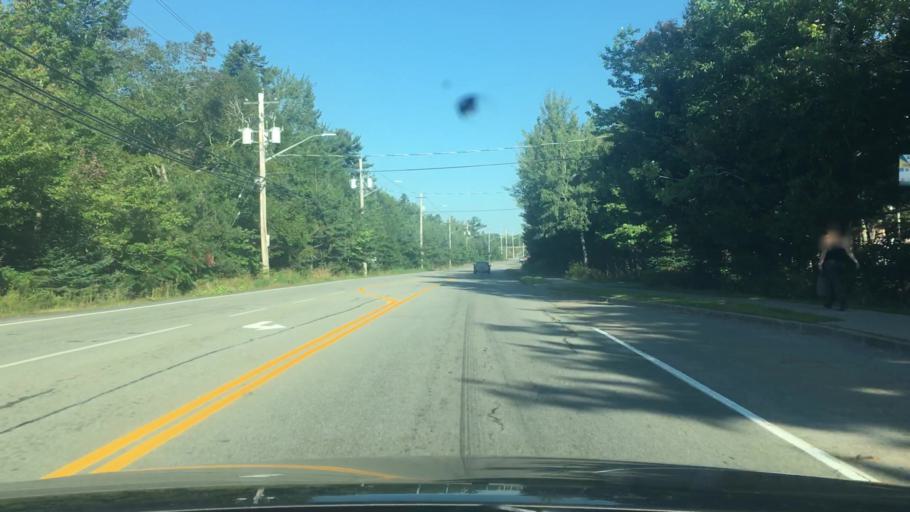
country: CA
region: Nova Scotia
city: Dartmouth
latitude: 44.7189
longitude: -63.6856
